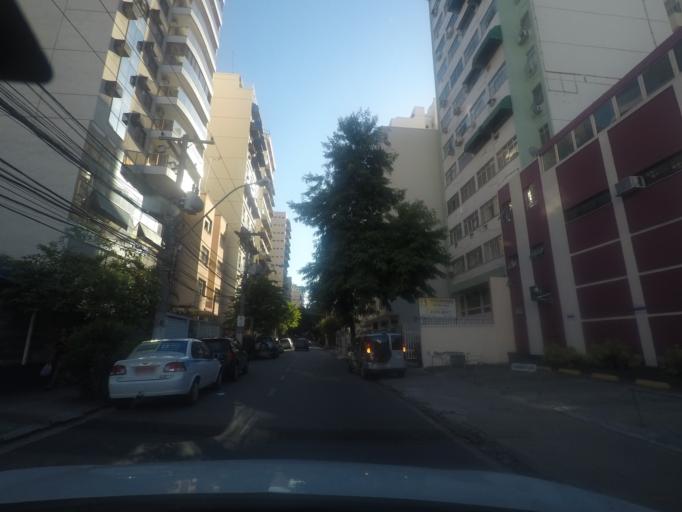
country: BR
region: Rio de Janeiro
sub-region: Niteroi
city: Niteroi
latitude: -22.9009
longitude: -43.1094
